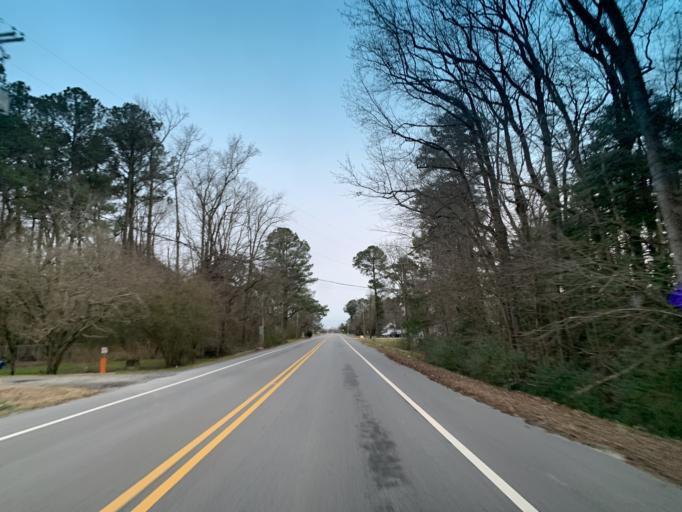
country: US
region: Maryland
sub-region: Worcester County
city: Pocomoke City
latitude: 38.0718
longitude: -75.5465
